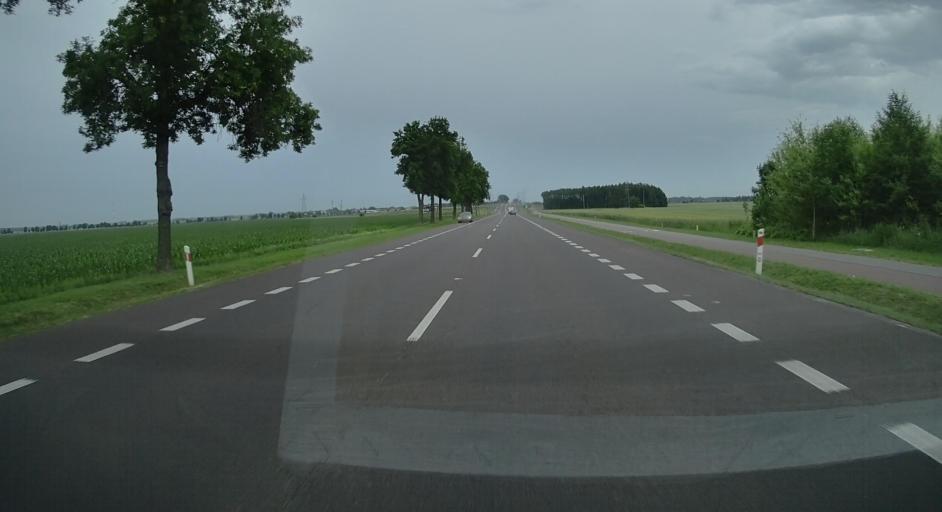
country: PL
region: Lublin Voivodeship
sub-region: Powiat bialski
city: Miedzyrzec Podlaski
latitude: 52.0078
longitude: 22.7454
